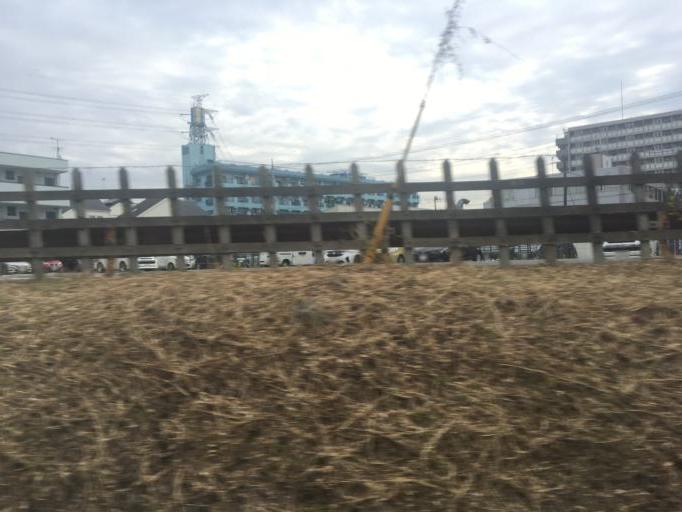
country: JP
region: Tokyo
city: Hachioji
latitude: 35.6662
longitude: 139.3615
